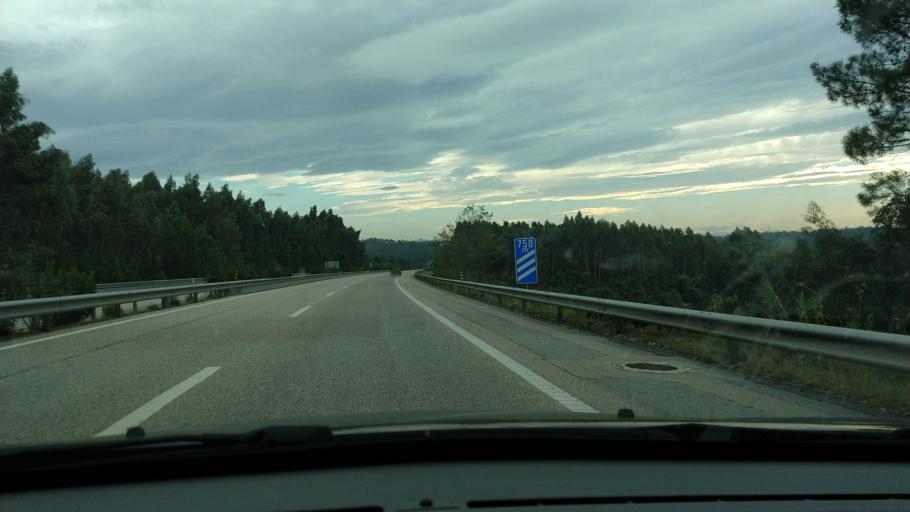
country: PT
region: Coimbra
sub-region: Figueira da Foz
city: Alhadas
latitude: 40.1534
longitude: -8.8041
